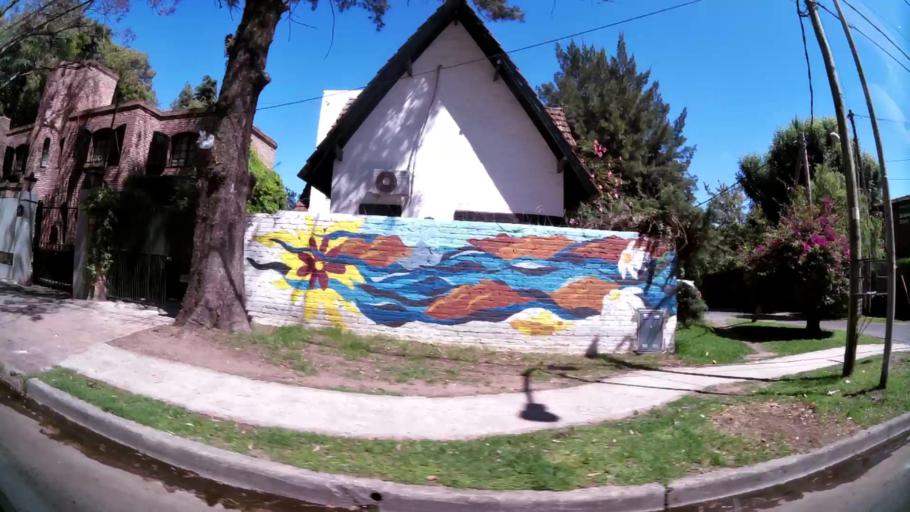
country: AR
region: Buenos Aires
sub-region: Partido de Tigre
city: Tigre
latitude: -34.4997
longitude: -58.6172
